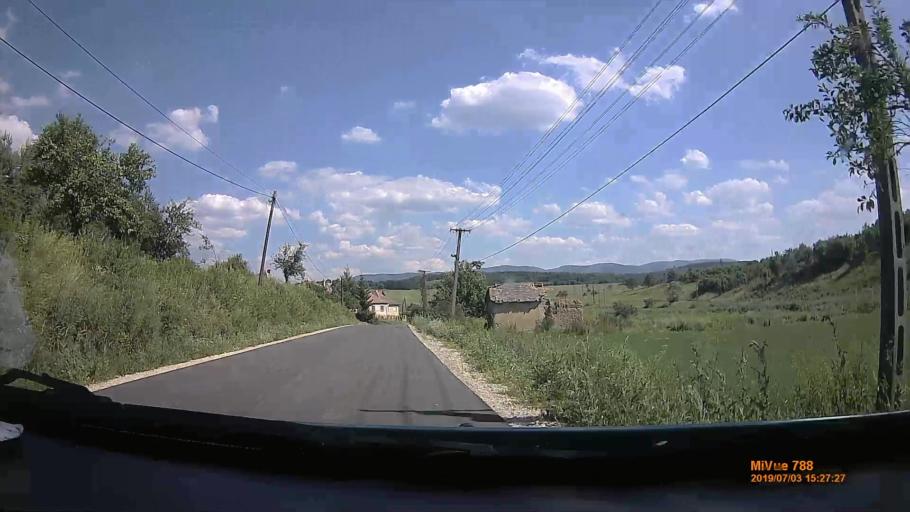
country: HU
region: Borsod-Abauj-Zemplen
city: Farkaslyuk
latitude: 48.1793
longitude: 20.3943
